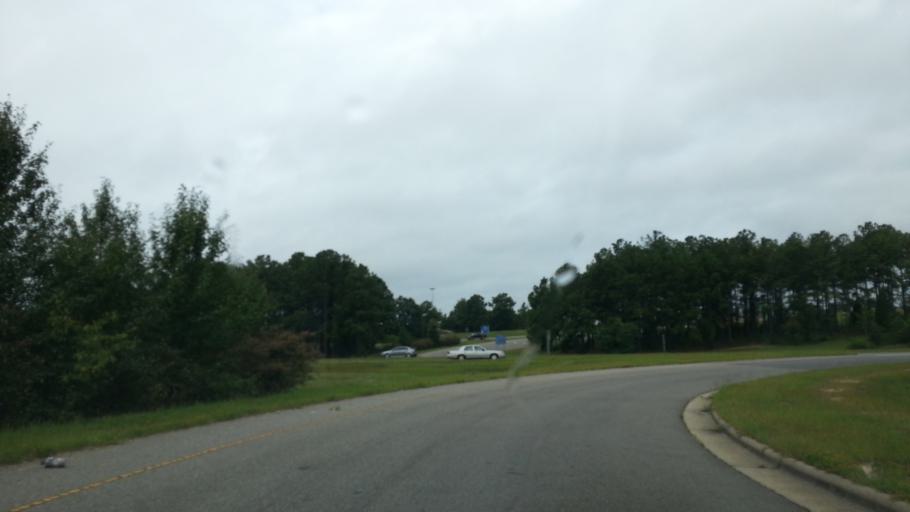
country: US
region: North Carolina
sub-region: Cumberland County
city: Fort Bragg
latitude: 35.0766
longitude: -78.9583
